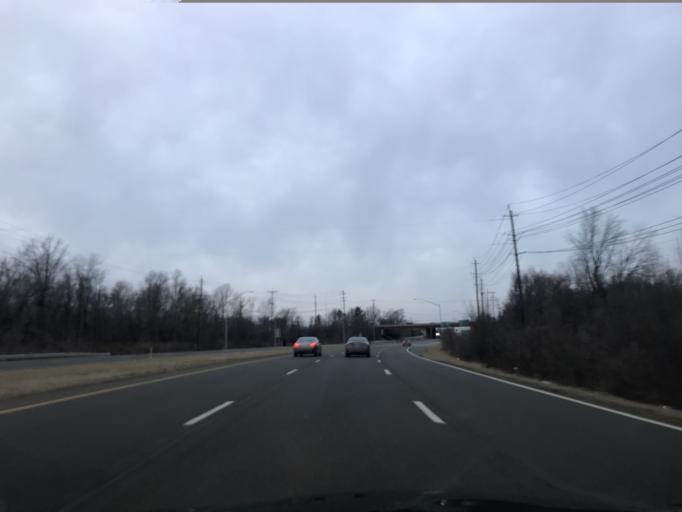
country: US
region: Maryland
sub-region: Prince George's County
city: Largo
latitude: 38.8953
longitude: -76.8303
